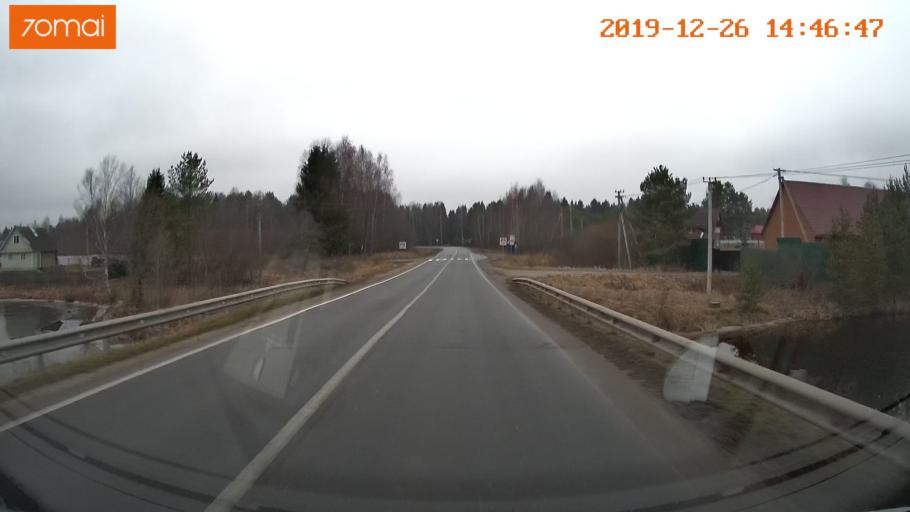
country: RU
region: Jaroslavl
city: Poshekhon'ye
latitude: 58.3394
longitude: 39.0119
